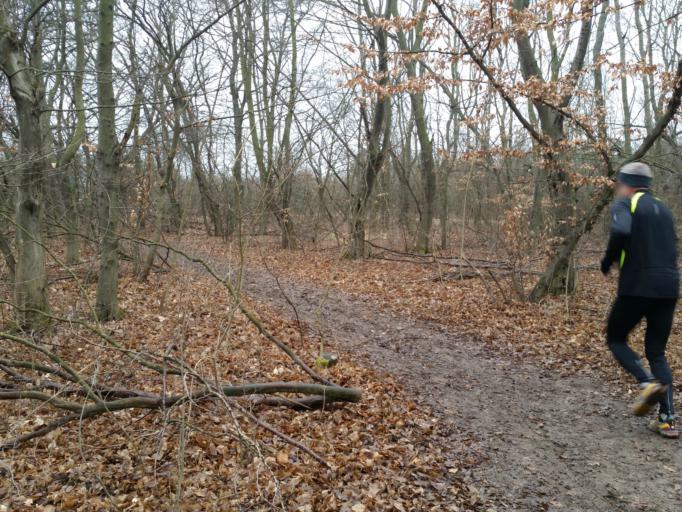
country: HU
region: Budapest
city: Budapest II. keruelet
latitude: 47.5444
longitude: 18.9936
